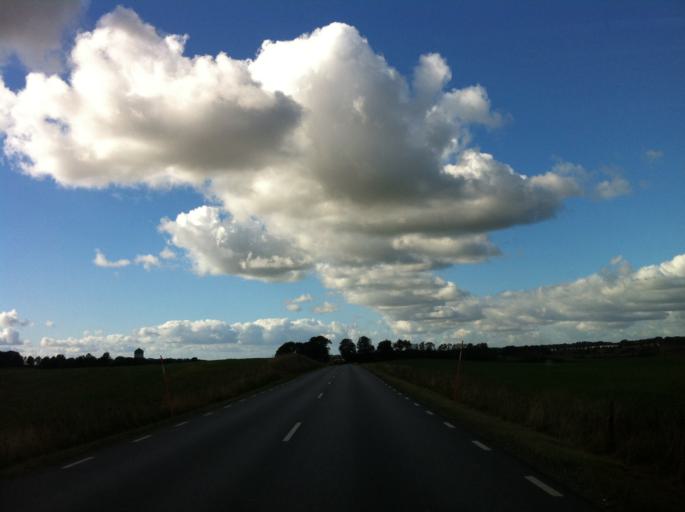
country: SE
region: Skane
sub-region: Tomelilla Kommun
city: Tomelilla
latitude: 55.6430
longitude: 13.9953
